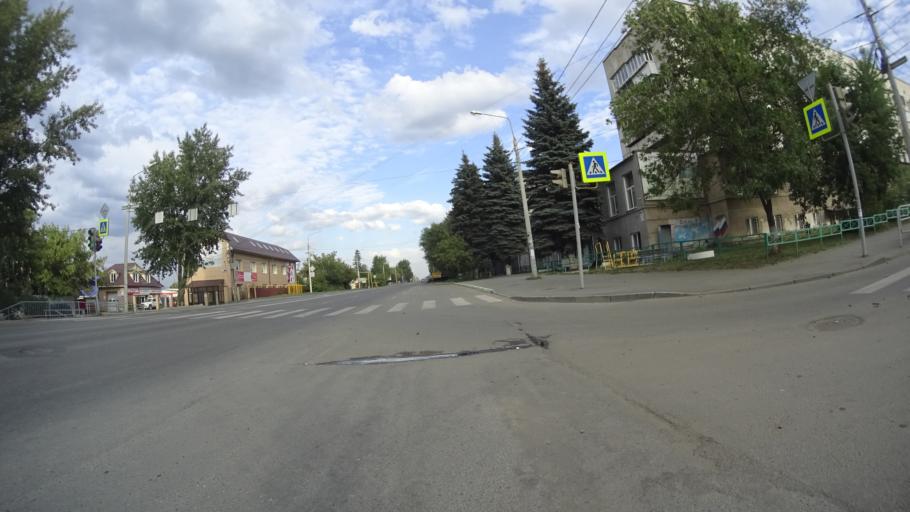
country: RU
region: Chelyabinsk
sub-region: Gorod Chelyabinsk
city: Chelyabinsk
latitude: 55.1984
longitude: 61.3544
